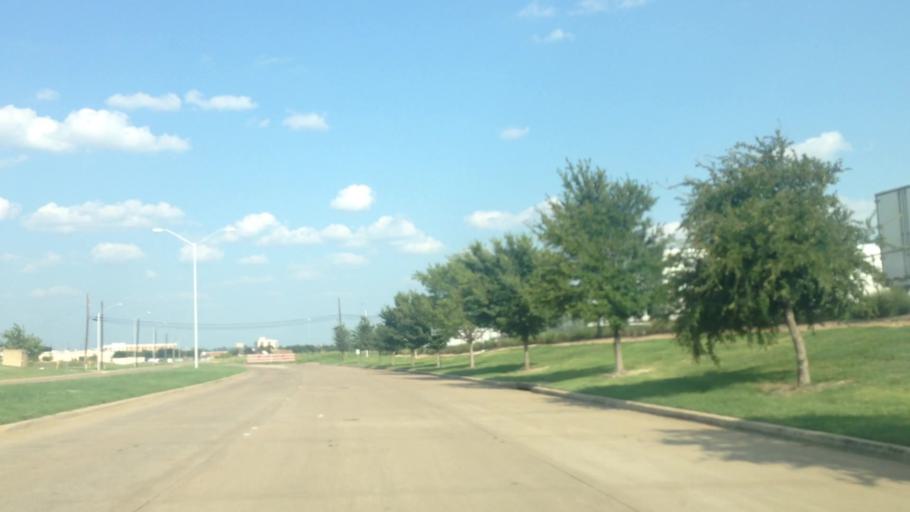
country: US
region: Texas
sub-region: Tarrant County
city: Blue Mound
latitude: 32.8245
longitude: -97.3274
